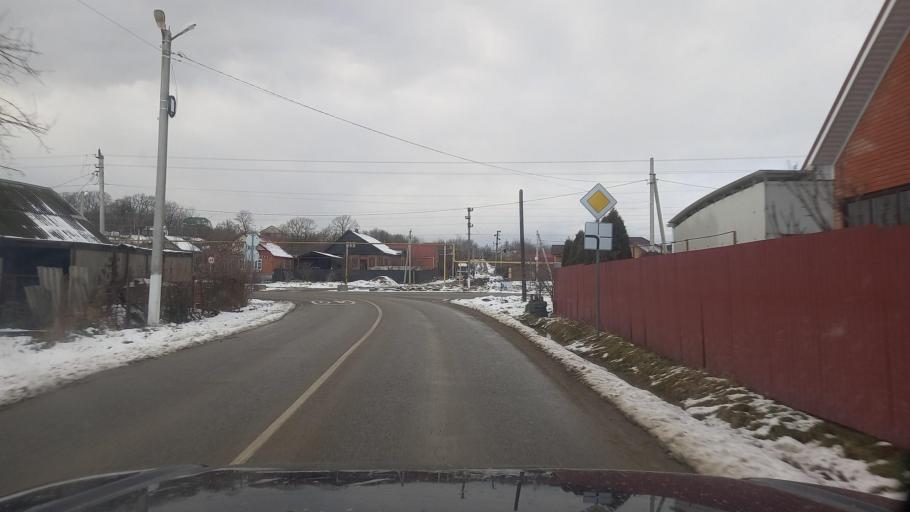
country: RU
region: Krasnodarskiy
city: Smolenskaya
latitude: 44.7752
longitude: 38.7875
